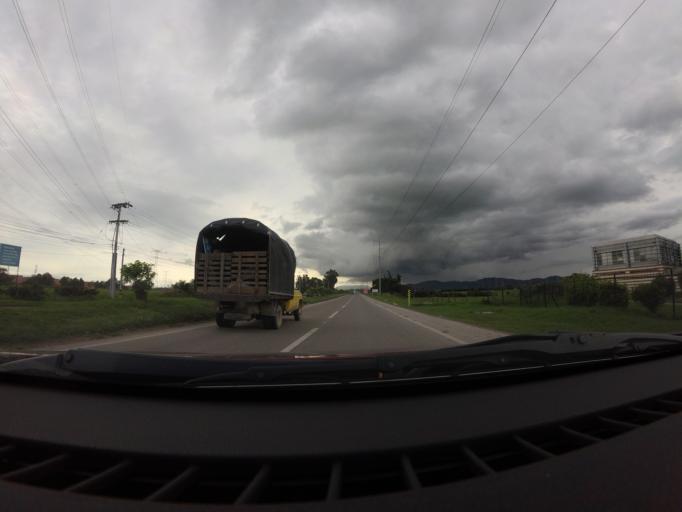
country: CO
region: Cundinamarca
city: Funza
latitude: 4.7698
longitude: -74.1708
